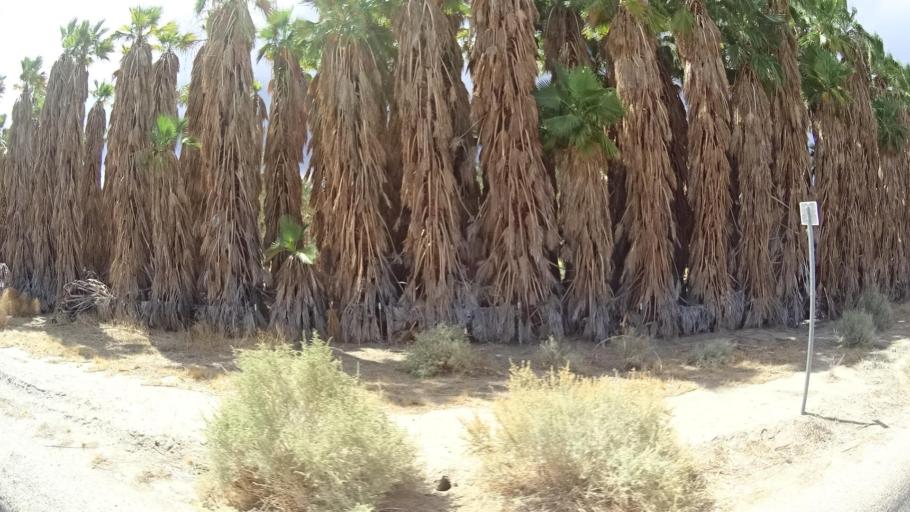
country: US
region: California
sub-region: San Diego County
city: Borrego Springs
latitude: 33.2761
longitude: -116.3487
